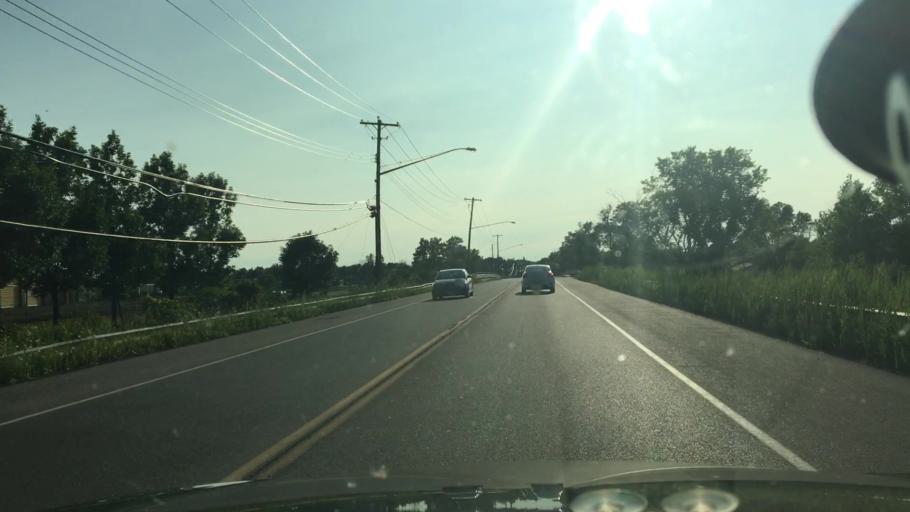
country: US
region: New York
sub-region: Erie County
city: Blasdell
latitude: 42.7970
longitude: -78.8145
